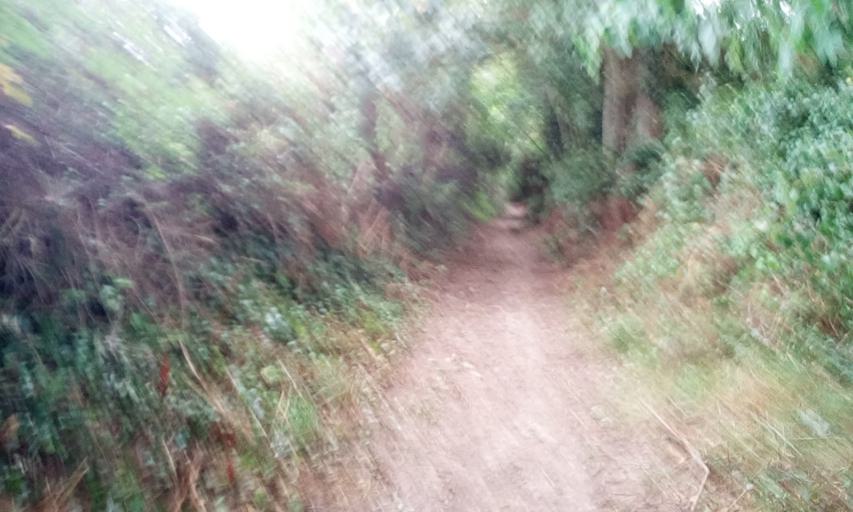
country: FR
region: Lower Normandy
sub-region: Departement du Calvados
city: Tourville-sur-Odon
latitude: 49.1339
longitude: -0.4907
